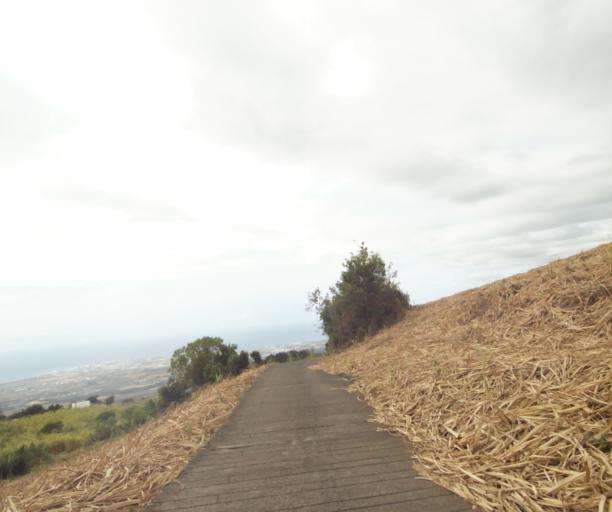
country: RE
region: Reunion
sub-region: Reunion
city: Saint-Paul
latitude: -21.0200
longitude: 55.3253
